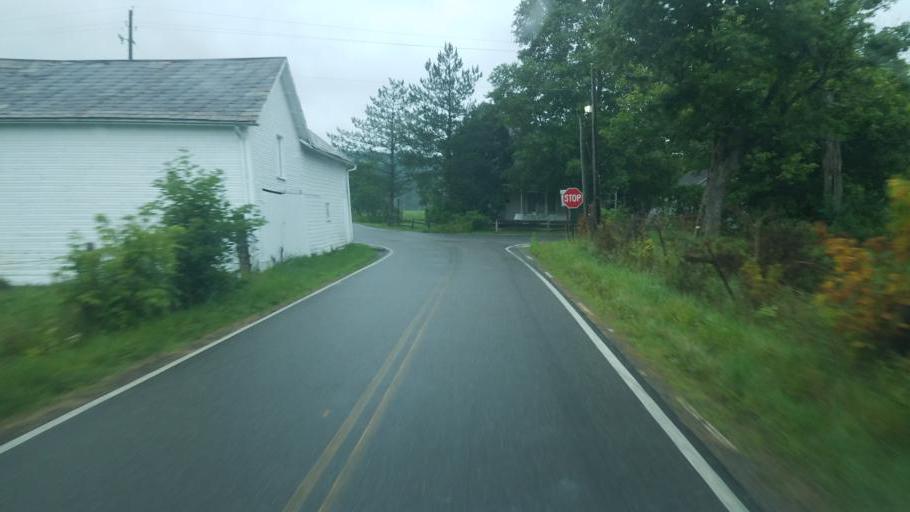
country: US
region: Ohio
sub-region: Tuscarawas County
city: Dennison
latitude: 40.3719
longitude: -81.2390
